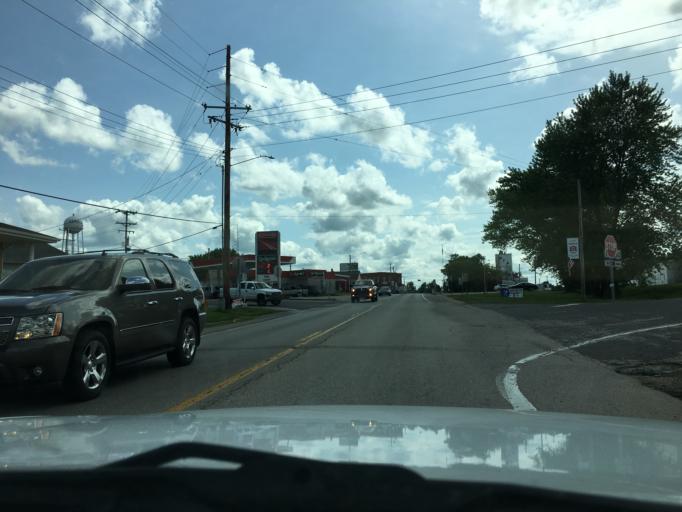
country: US
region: Missouri
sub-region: Franklin County
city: Gerald
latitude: 38.4025
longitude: -91.3289
